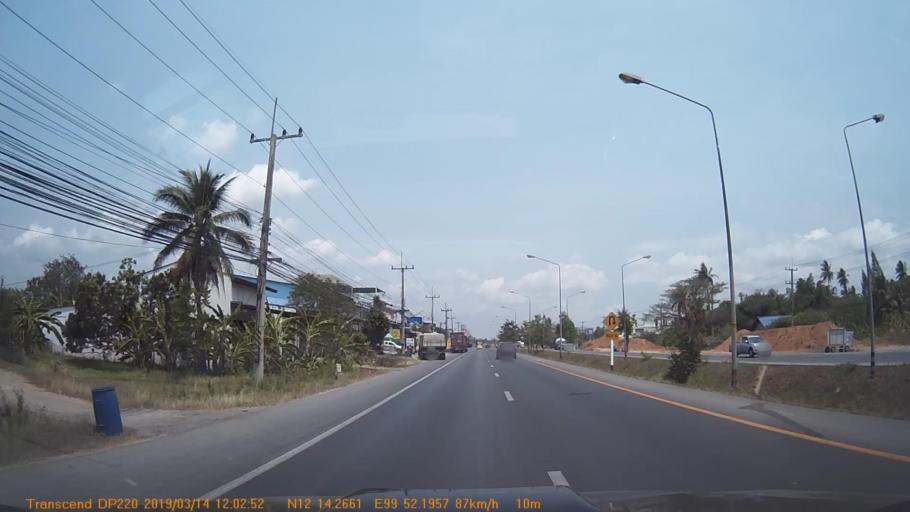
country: TH
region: Prachuap Khiri Khan
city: Sam Roi Yot
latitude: 12.2382
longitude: 99.8700
